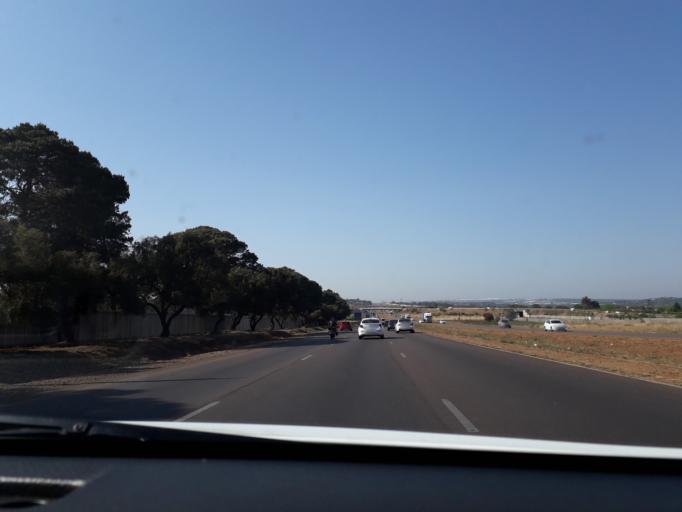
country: ZA
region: Gauteng
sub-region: City of Tshwane Metropolitan Municipality
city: Centurion
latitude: -25.8037
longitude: 28.1807
